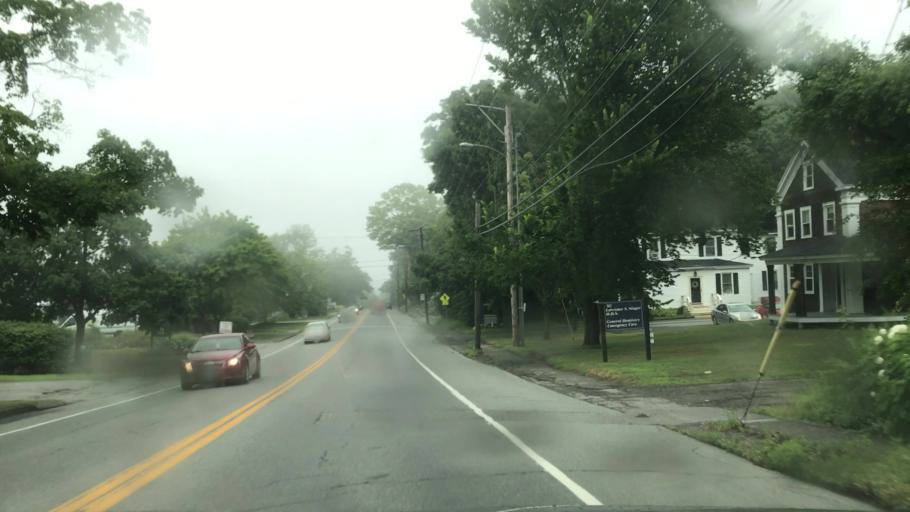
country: US
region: Maine
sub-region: Knox County
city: Camden
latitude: 44.2047
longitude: -69.0717
